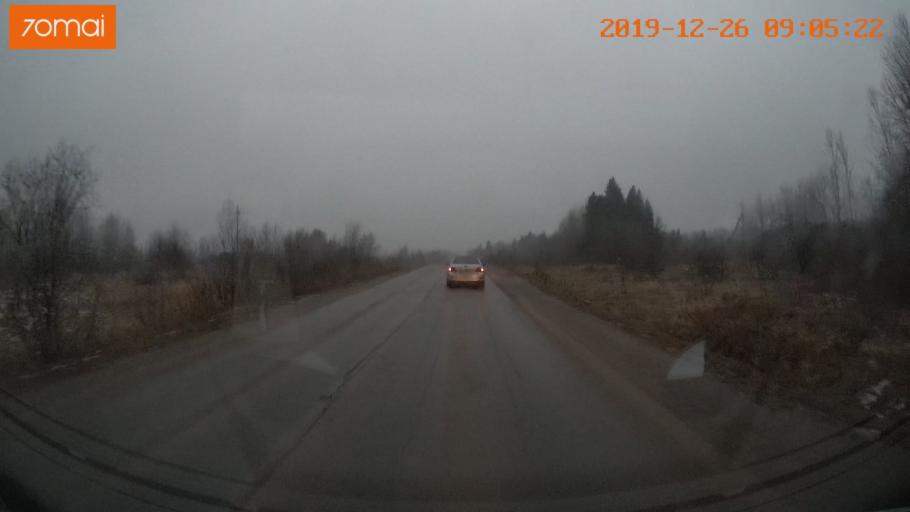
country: RU
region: Vologda
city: Gryazovets
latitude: 58.8248
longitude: 40.2581
